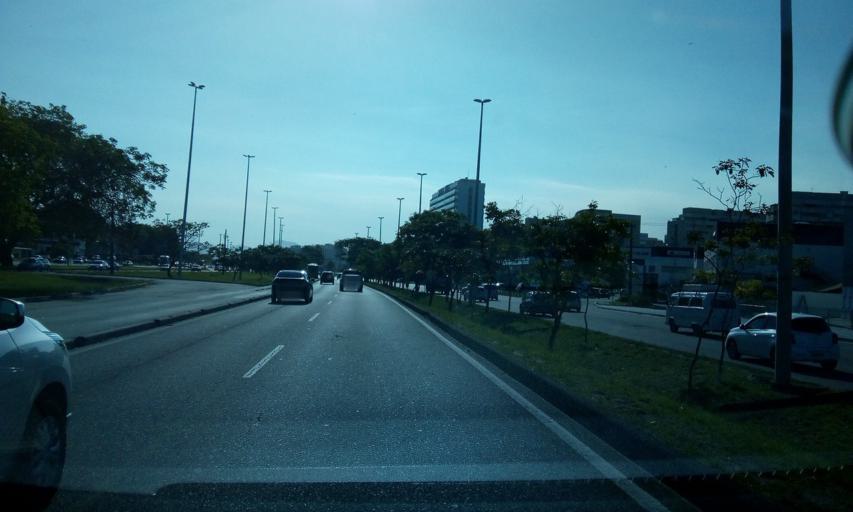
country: BR
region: Rio de Janeiro
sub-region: Nilopolis
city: Nilopolis
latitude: -23.0000
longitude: -43.4131
